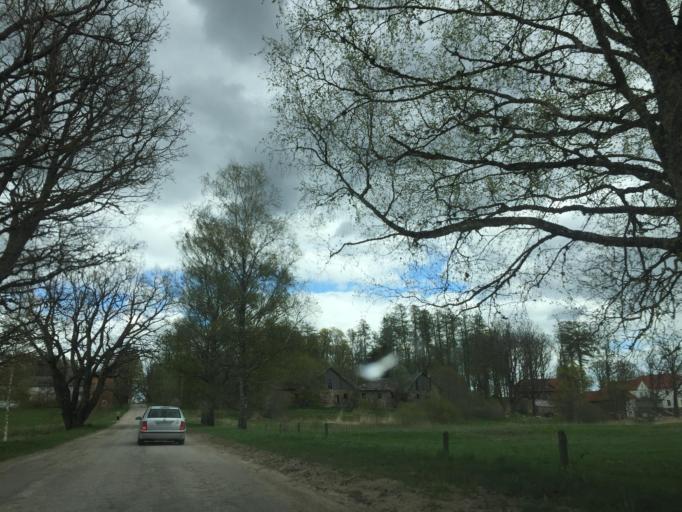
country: LV
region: Madonas Rajons
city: Madona
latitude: 56.9230
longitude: 26.0521
